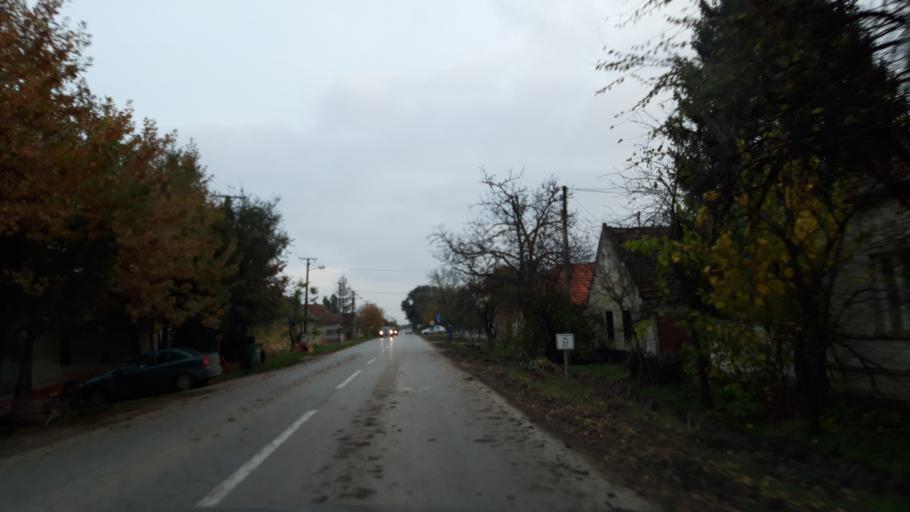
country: RS
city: Sanad
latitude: 45.9804
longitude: 20.1133
